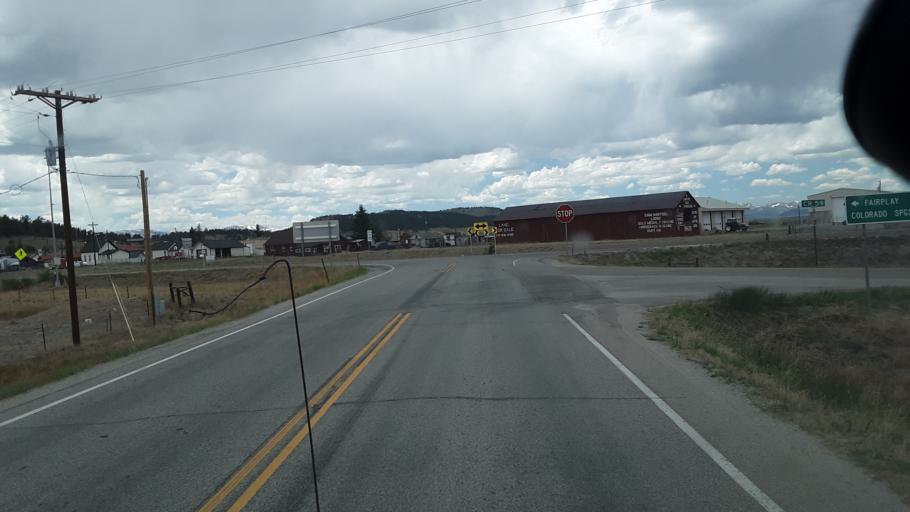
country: US
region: Colorado
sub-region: Park County
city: Fairplay
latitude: 39.0210
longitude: -105.7932
